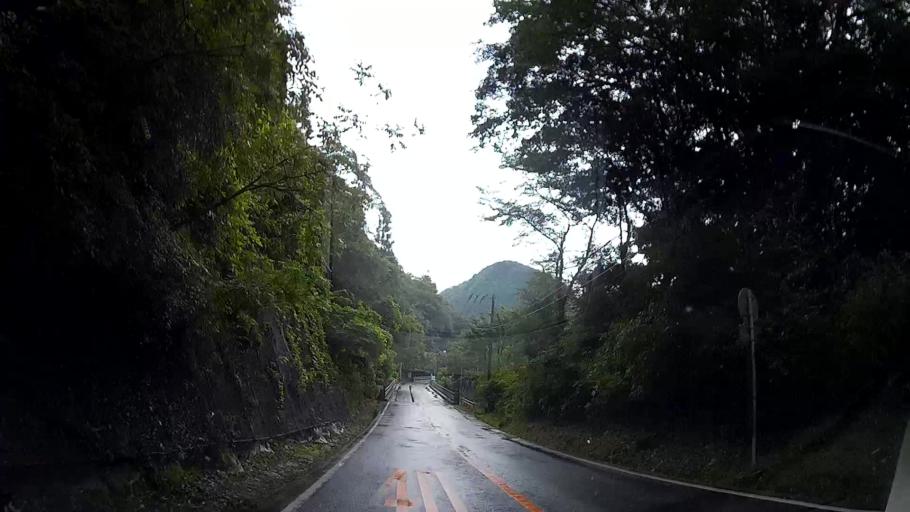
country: JP
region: Oita
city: Hita
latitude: 33.1819
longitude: 131.0031
